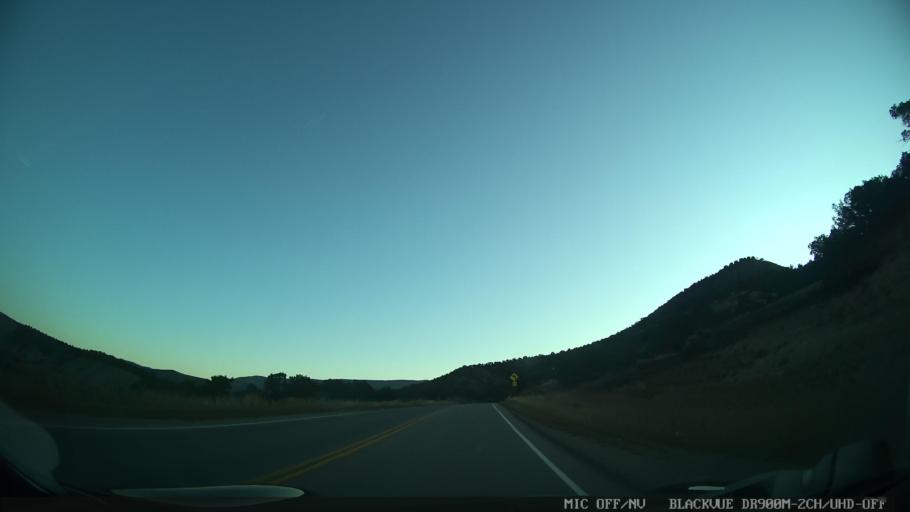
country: US
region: Colorado
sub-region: Eagle County
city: Edwards
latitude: 39.7203
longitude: -106.6812
